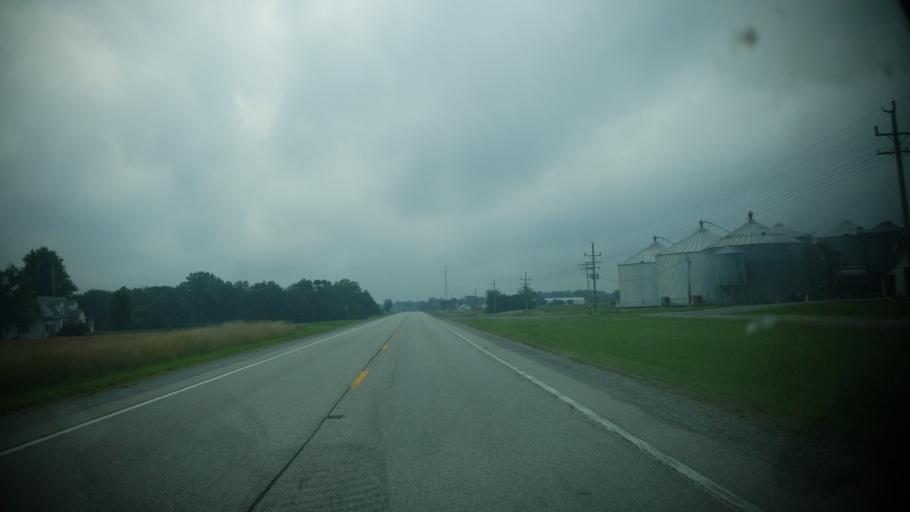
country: US
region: Illinois
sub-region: Clay County
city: Flora
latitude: 38.6778
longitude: -88.3738
